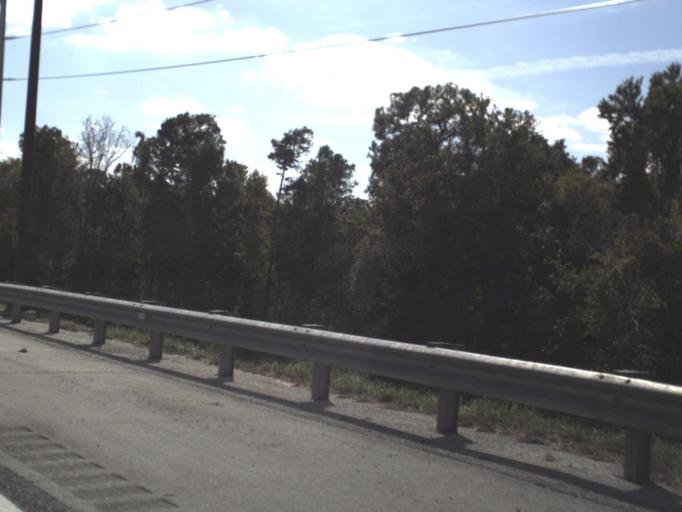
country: US
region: Florida
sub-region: Polk County
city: Citrus Ridge
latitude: 28.3012
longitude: -81.6071
